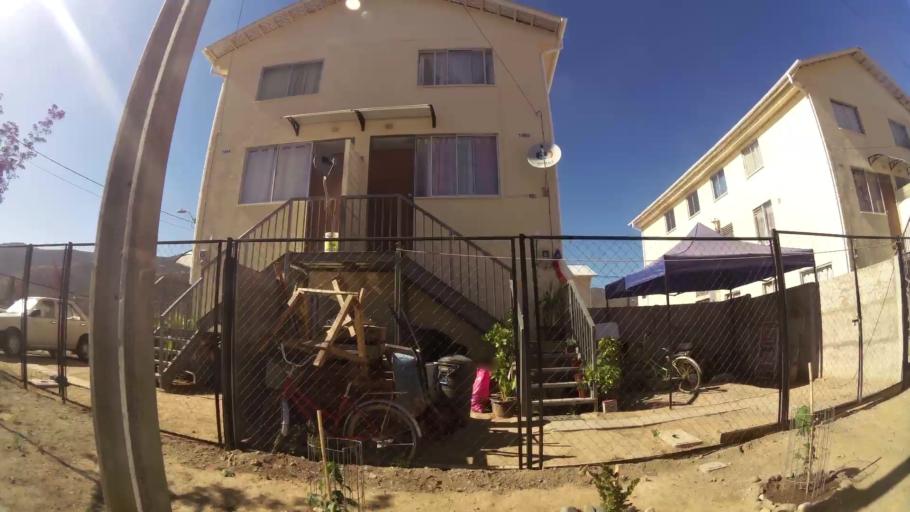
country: CL
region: Santiago Metropolitan
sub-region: Provincia de Chacabuco
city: Lampa
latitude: -33.4083
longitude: -71.1268
